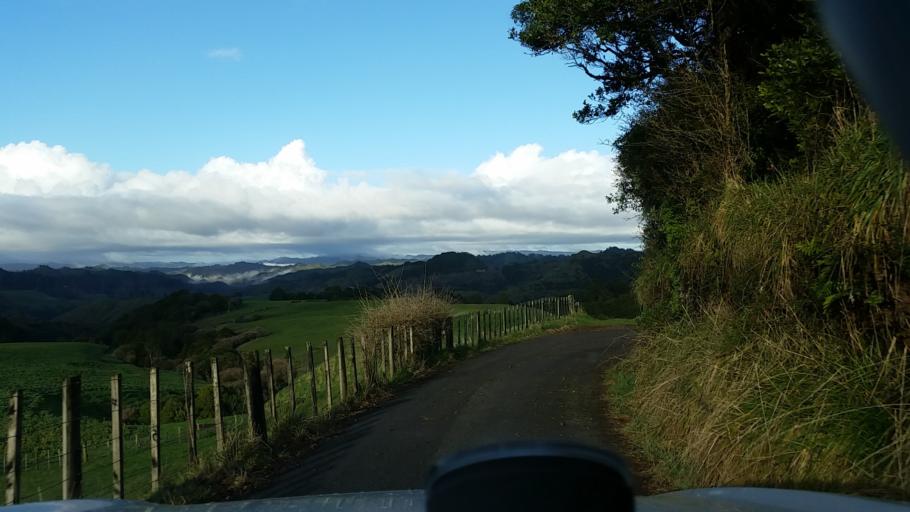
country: NZ
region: Taranaki
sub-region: South Taranaki District
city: Eltham
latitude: -39.4097
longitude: 174.5703
